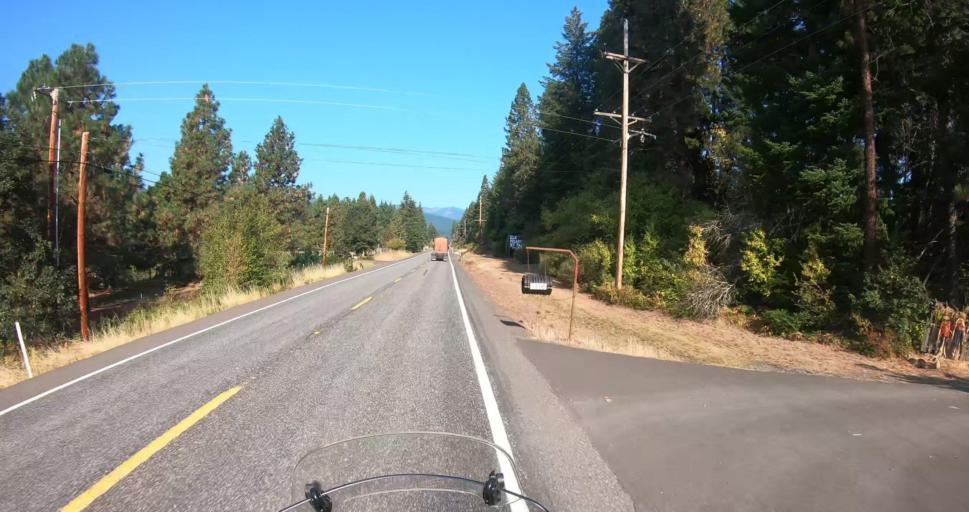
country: US
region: Washington
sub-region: Klickitat County
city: White Salmon
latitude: 45.8316
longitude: -121.4948
